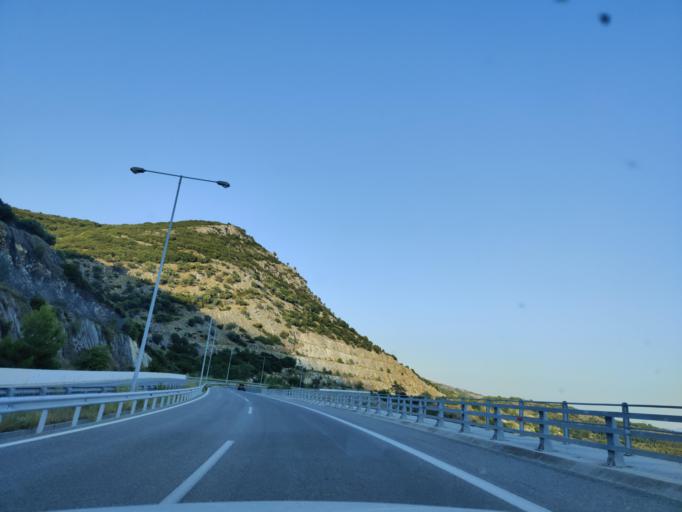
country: GR
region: East Macedonia and Thrace
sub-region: Nomos Kavalas
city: Kavala
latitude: 40.9666
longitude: 24.4165
